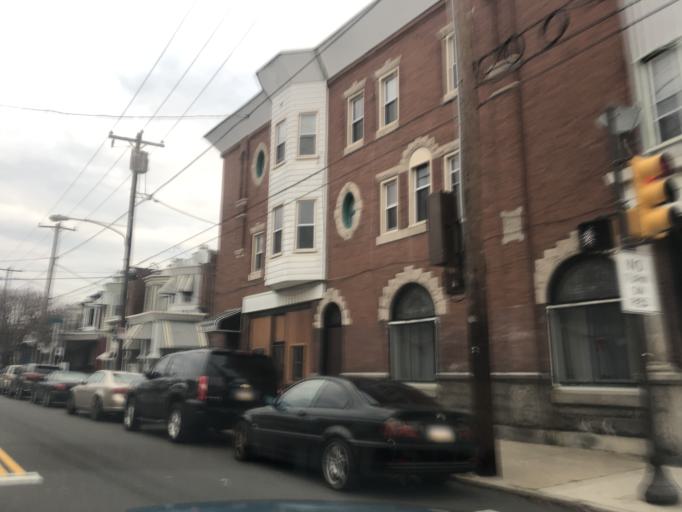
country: US
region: Pennsylvania
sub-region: Delaware County
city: Millbourne
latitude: 39.9685
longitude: -75.2354
